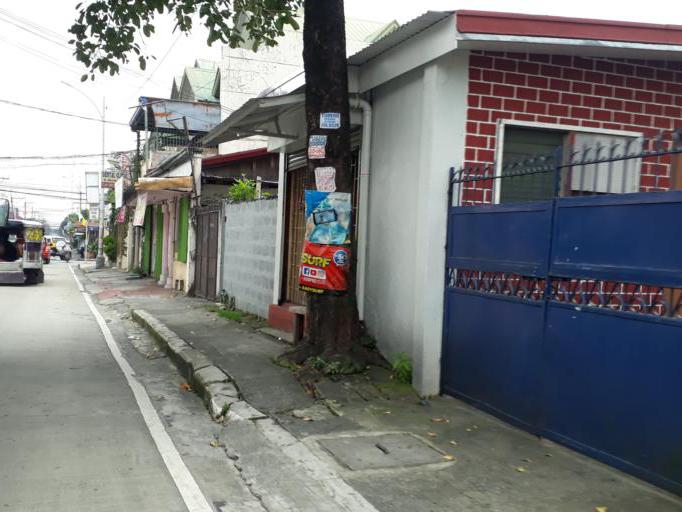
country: PH
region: Calabarzon
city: Bagong Pagasa
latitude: 14.6602
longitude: 121.0412
